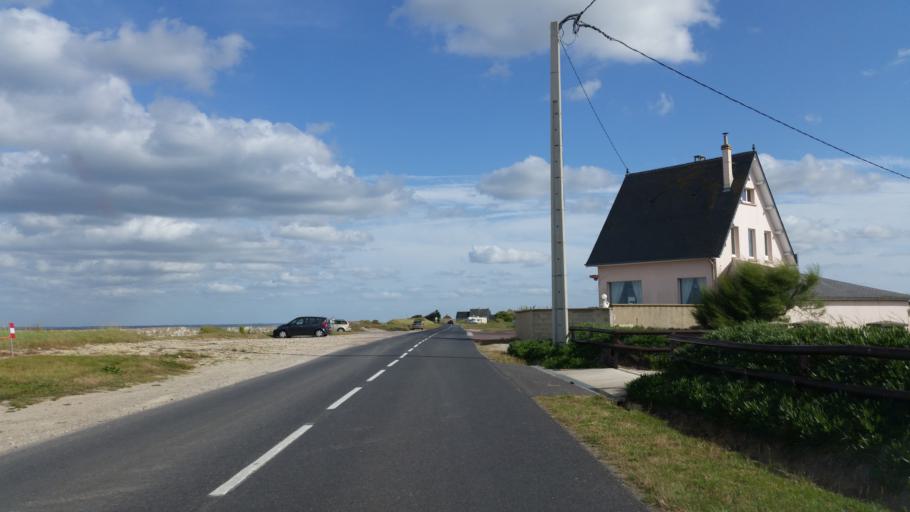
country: FR
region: Lower Normandy
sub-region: Departement de la Manche
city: Sainte-Mere-Eglise
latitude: 49.4538
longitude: -1.2207
